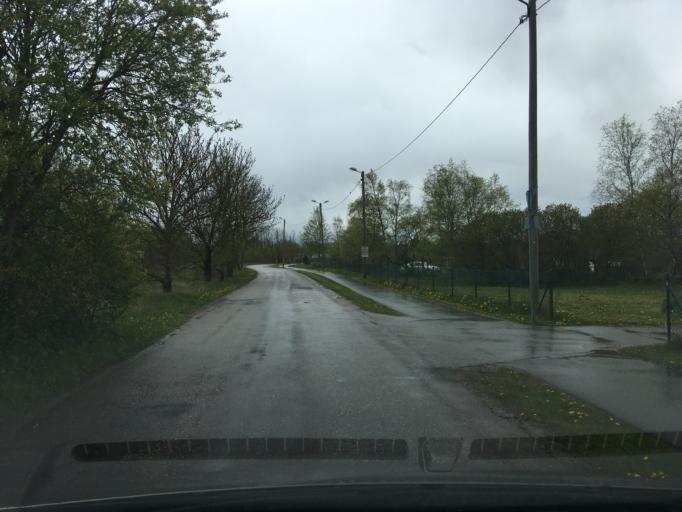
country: EE
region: Harju
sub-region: Joelaehtme vald
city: Loo
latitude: 59.4360
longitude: 24.9584
